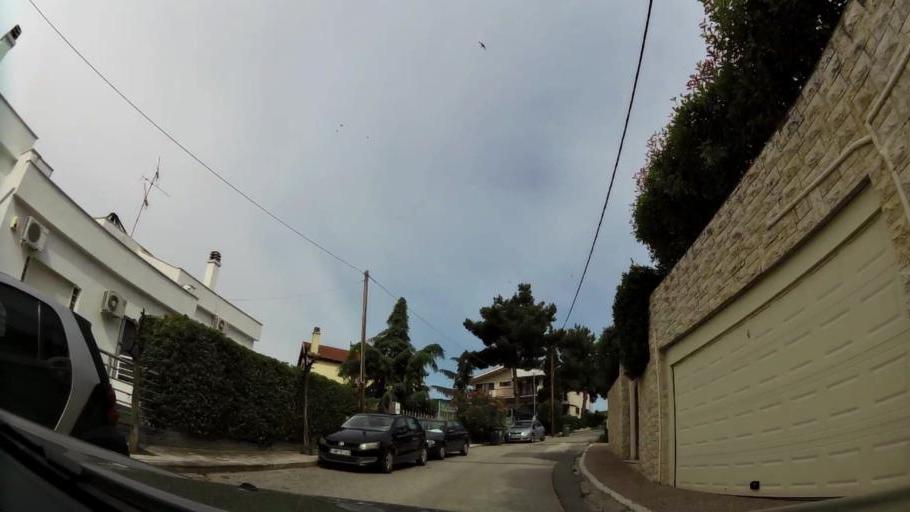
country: GR
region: Central Macedonia
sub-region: Nomos Thessalonikis
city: Panorama
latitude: 40.5883
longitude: 23.0219
